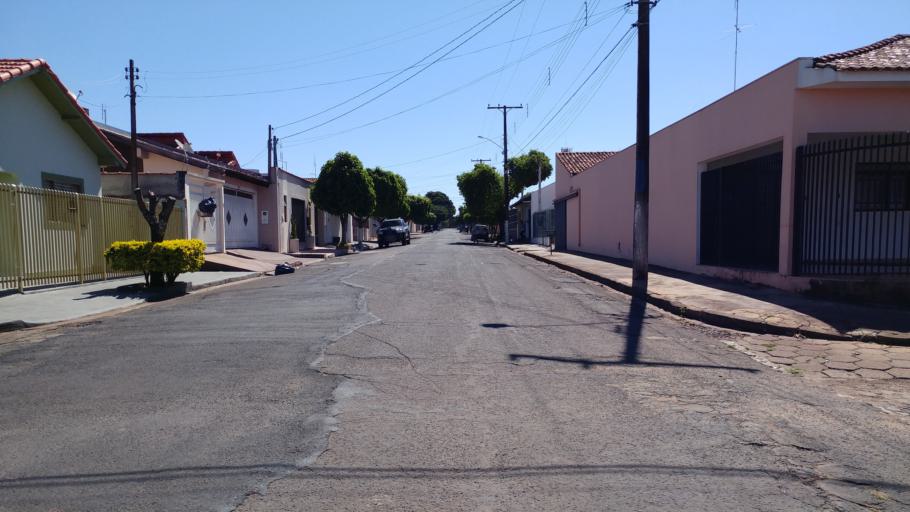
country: BR
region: Sao Paulo
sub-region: Paraguacu Paulista
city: Paraguacu Paulista
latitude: -22.4106
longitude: -50.5780
